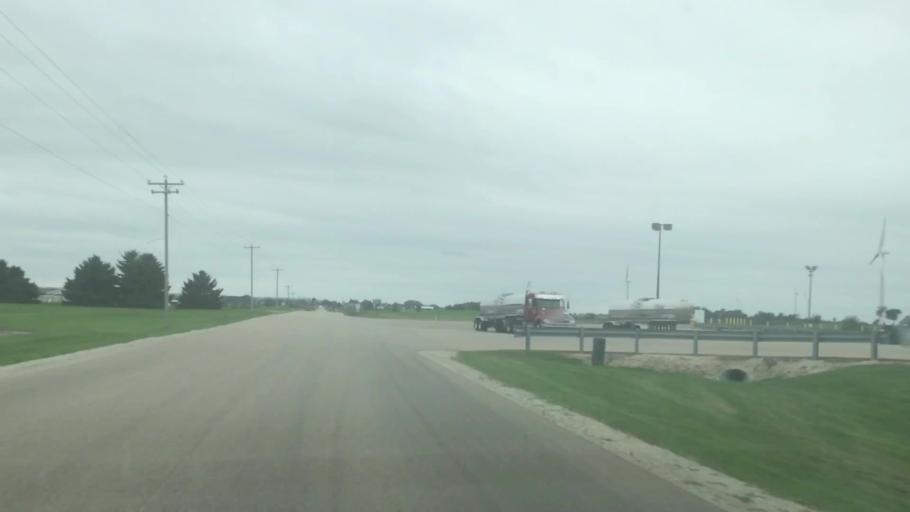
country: US
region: Wisconsin
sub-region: Fond du Lac County
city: Oakfield
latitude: 43.6157
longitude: -88.5416
